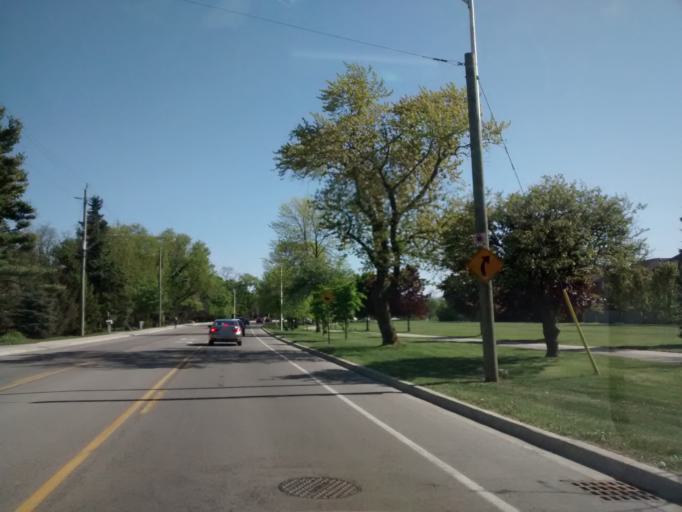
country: CA
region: Ontario
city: Oakville
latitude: 43.3797
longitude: -79.7174
